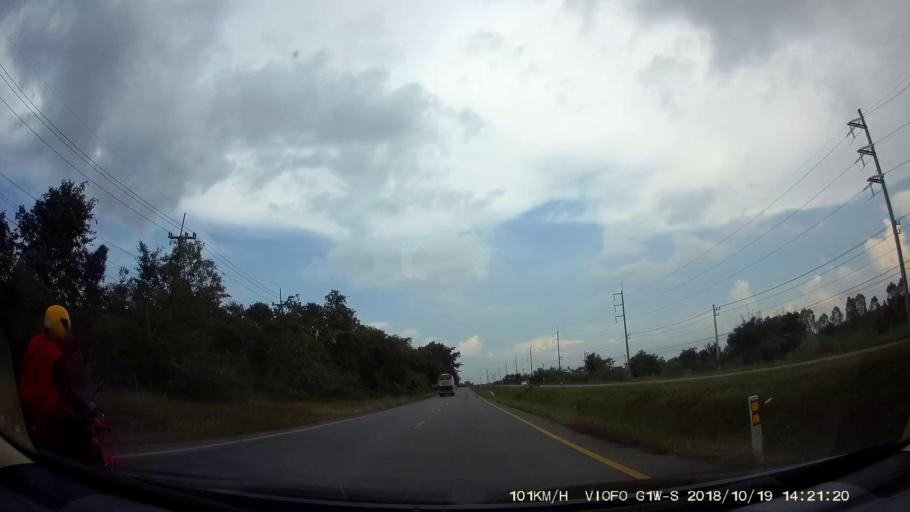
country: TH
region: Chaiyaphum
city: Kaeng Khro
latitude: 16.0512
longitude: 102.2653
